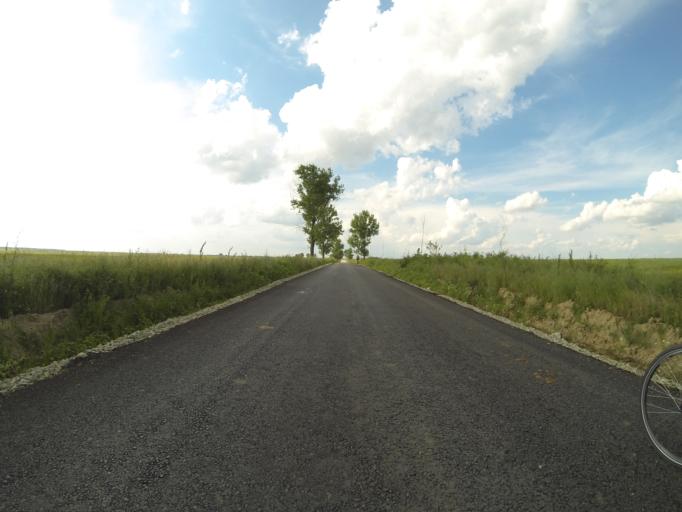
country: RO
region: Dolj
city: Satu Nou Calopar
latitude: 44.1386
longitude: 23.7949
